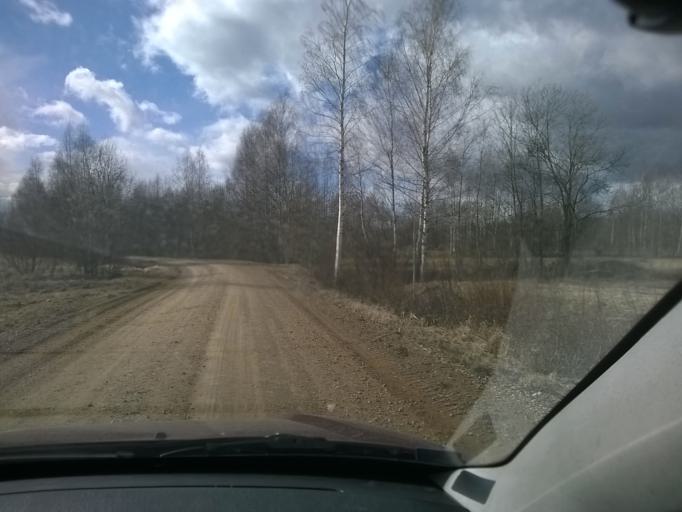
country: EE
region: Tartu
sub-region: Alatskivi vald
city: Kallaste
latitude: 58.3817
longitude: 27.0861
